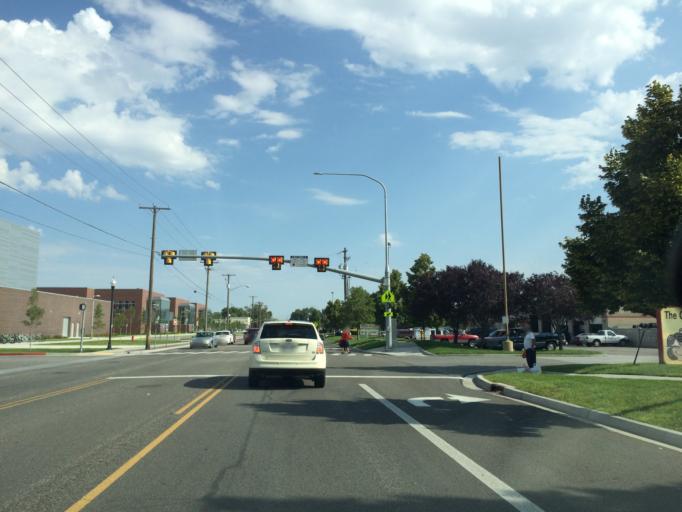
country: US
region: Utah
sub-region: Salt Lake County
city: West Valley City
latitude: 40.6940
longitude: -111.9770
